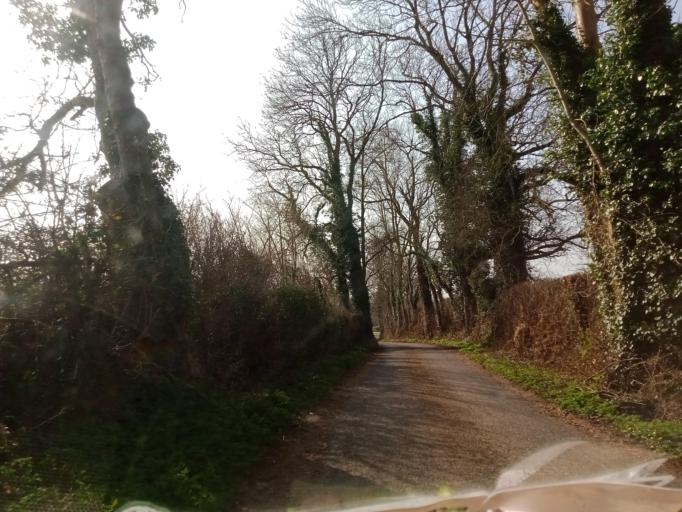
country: IE
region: Leinster
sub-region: Kilkenny
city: Callan
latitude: 52.5292
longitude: -7.3999
